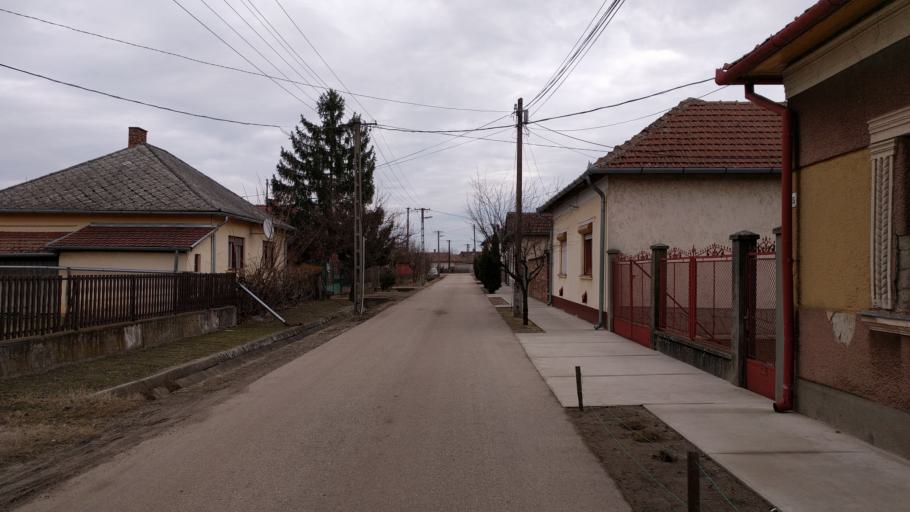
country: HU
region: Bacs-Kiskun
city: Tiszakecske
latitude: 46.9303
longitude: 20.1047
